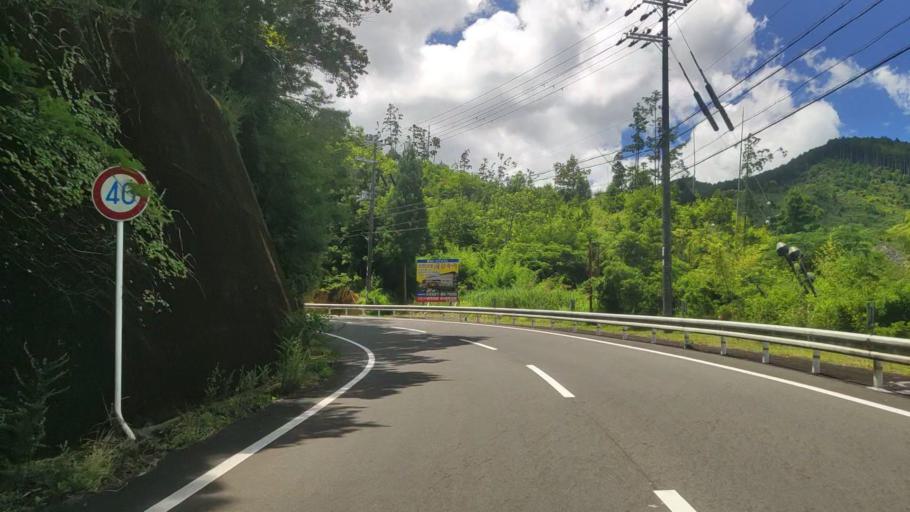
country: JP
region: Mie
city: Owase
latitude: 33.9552
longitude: 136.0690
